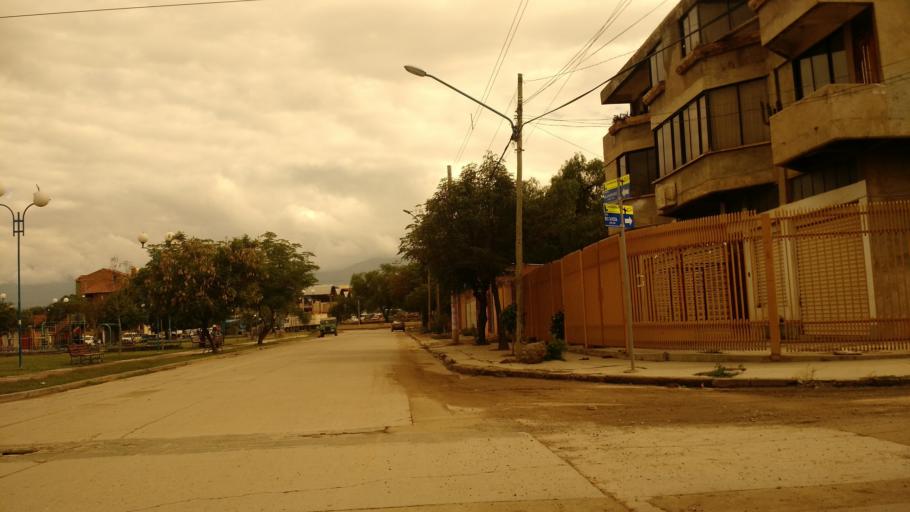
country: BO
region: Cochabamba
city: Cochabamba
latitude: -17.4311
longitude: -66.1555
